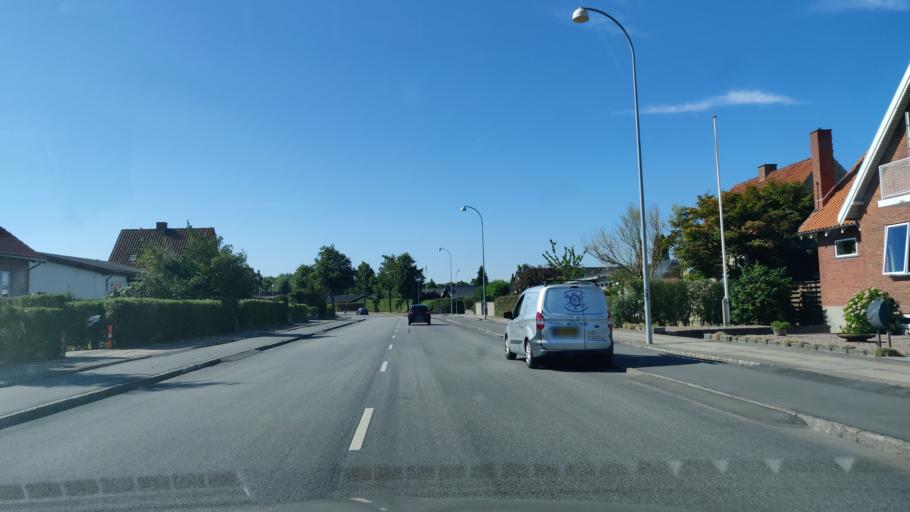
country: DK
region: Zealand
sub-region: Roskilde Kommune
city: Roskilde
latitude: 55.6348
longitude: 12.1016
